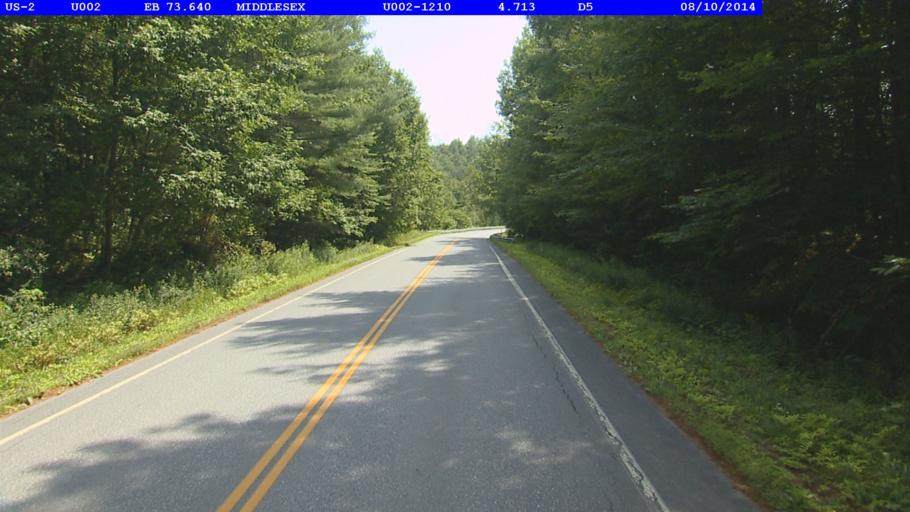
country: US
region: Vermont
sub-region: Washington County
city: Montpelier
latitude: 44.2685
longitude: -72.6258
